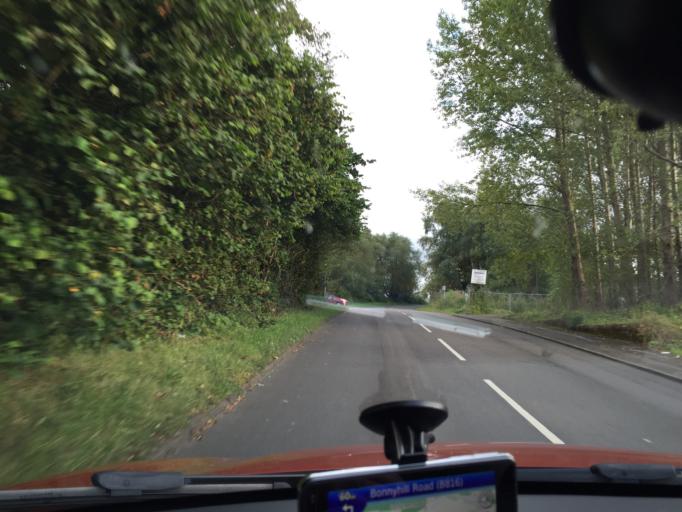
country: GB
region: Scotland
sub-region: Falkirk
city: Bonnybridge
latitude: 55.9916
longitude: -3.8744
